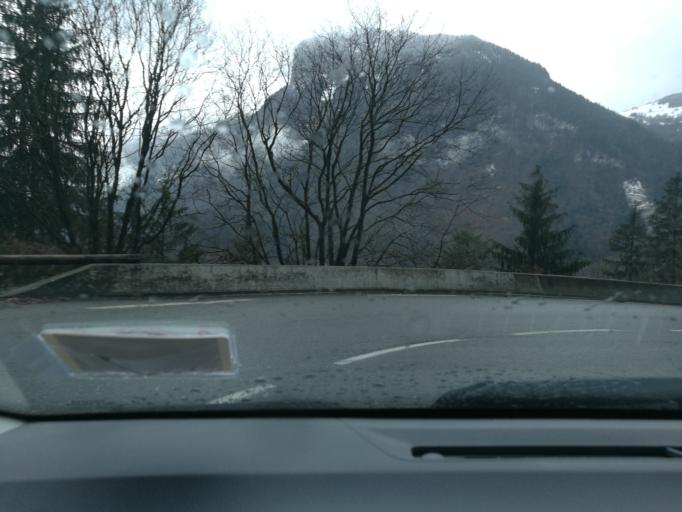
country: FR
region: Rhone-Alpes
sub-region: Departement de la Haute-Savoie
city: Araches-la-Frasse
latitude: 46.0429
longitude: 6.6159
